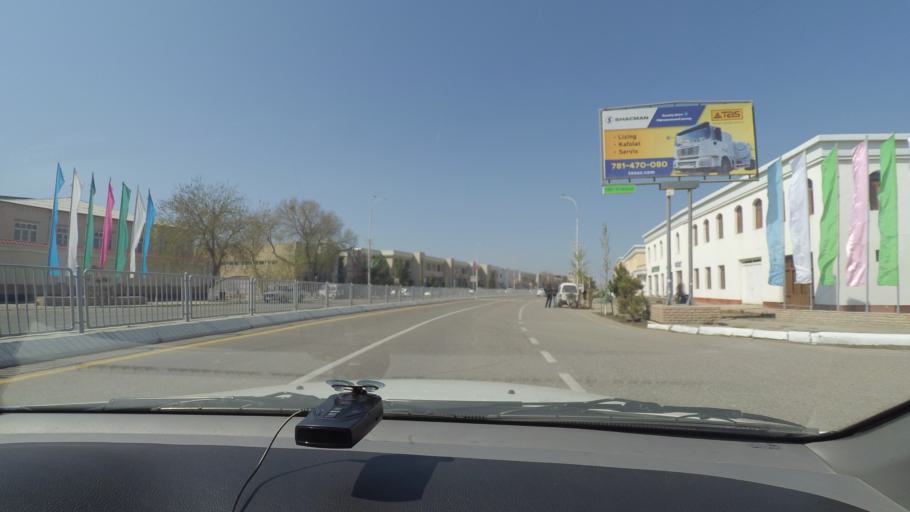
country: UZ
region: Bukhara
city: Bukhara
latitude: 39.7671
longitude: 64.4621
